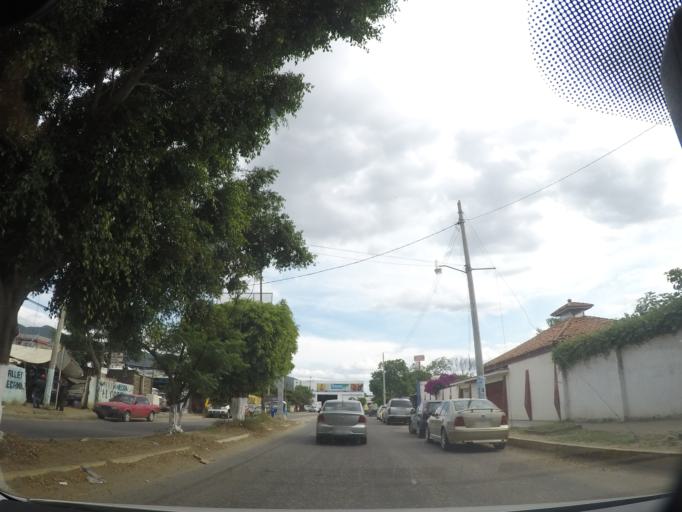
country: MX
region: Oaxaca
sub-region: Santa Cruz Amilpas
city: Santa Cruz Amilpas
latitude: 17.0648
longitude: -96.6797
